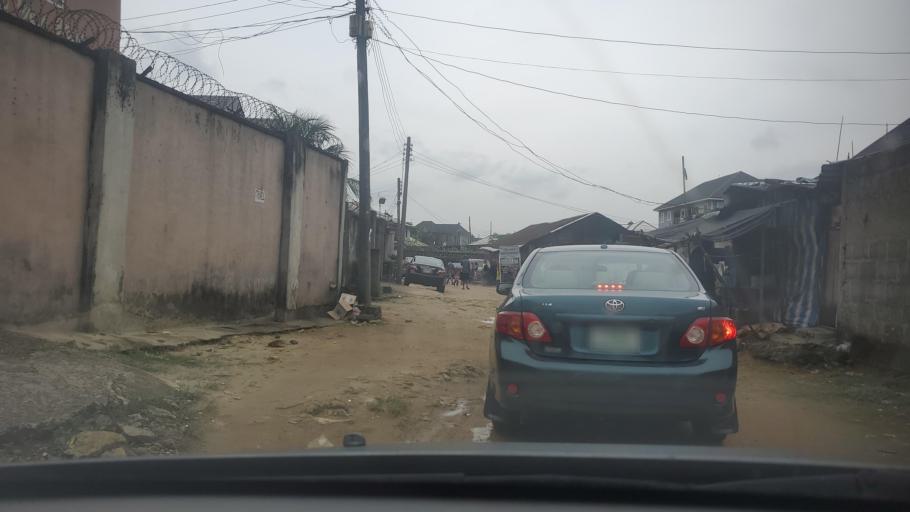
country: NG
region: Rivers
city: Port Harcourt
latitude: 4.8443
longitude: 7.0015
